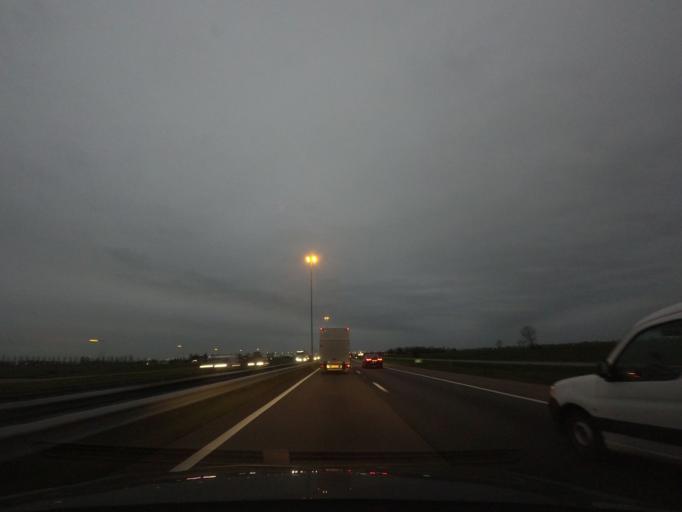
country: NL
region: South Holland
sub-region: Gemeente Gorinchem
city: Gorinchem
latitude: 51.9058
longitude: 4.9817
